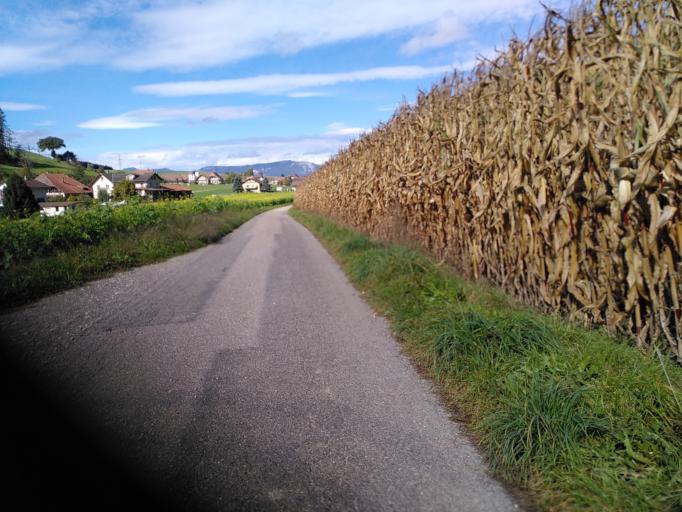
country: CH
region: Bern
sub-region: Oberaargau
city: Seeberg
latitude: 47.1368
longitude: 7.6746
